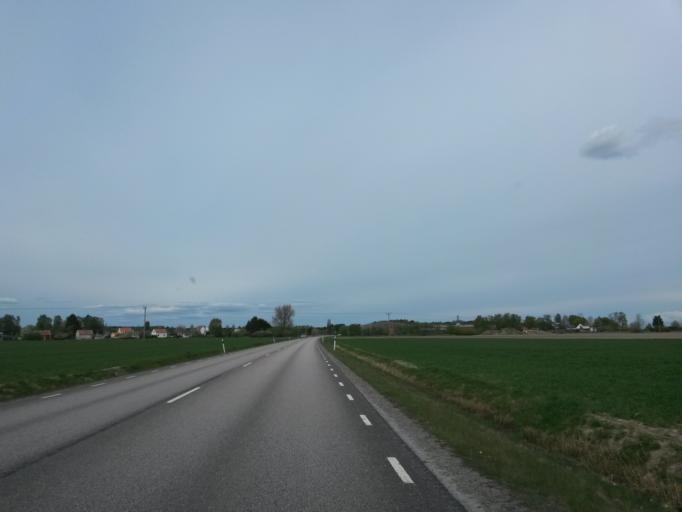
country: SE
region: Vaestra Goetaland
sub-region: Vara Kommun
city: Vara
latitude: 58.3189
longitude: 12.9350
